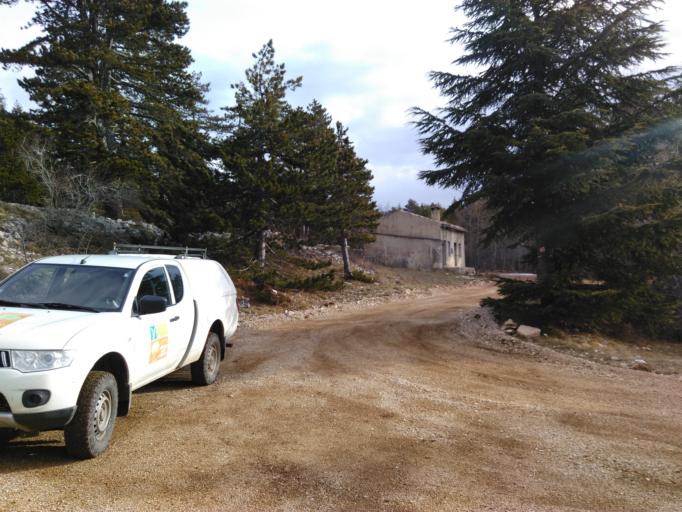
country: FR
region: Provence-Alpes-Cote d'Azur
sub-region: Departement du Vaucluse
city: Sault
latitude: 44.1378
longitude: 5.3344
